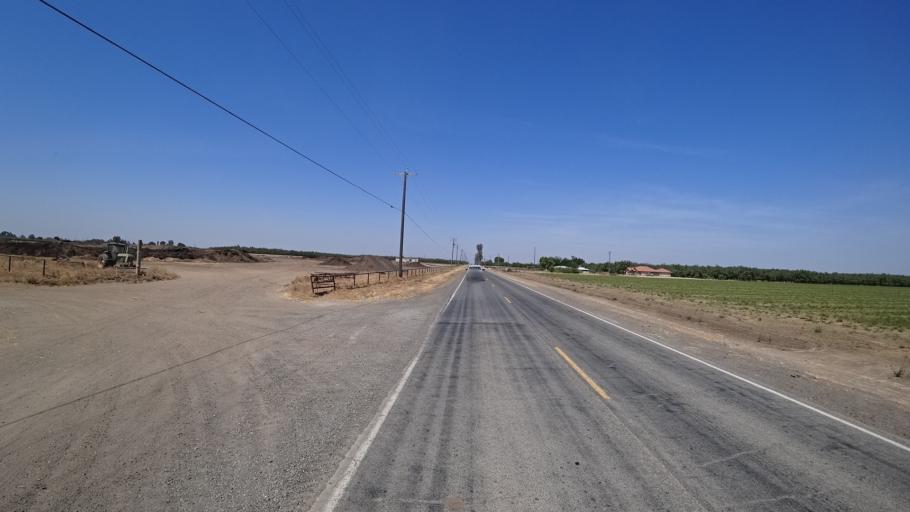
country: US
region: California
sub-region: Fresno County
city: Riverdale
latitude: 36.4020
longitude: -119.8190
